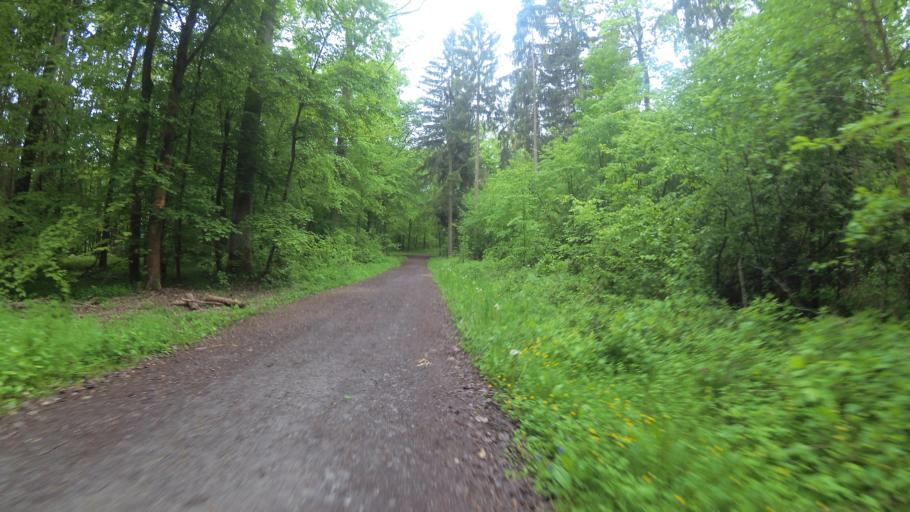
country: DE
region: Baden-Wuerttemberg
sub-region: Regierungsbezirk Stuttgart
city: Erlenbach
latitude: 49.1947
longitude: 9.2692
